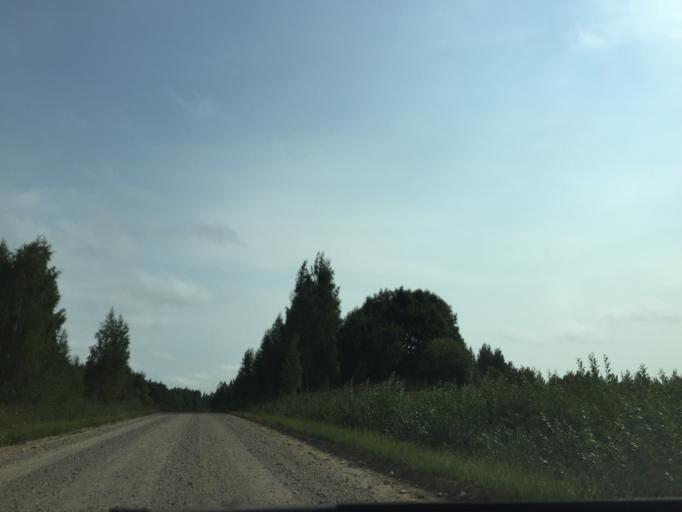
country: LV
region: Ludzas Rajons
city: Ludza
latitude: 56.2927
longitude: 27.7273
